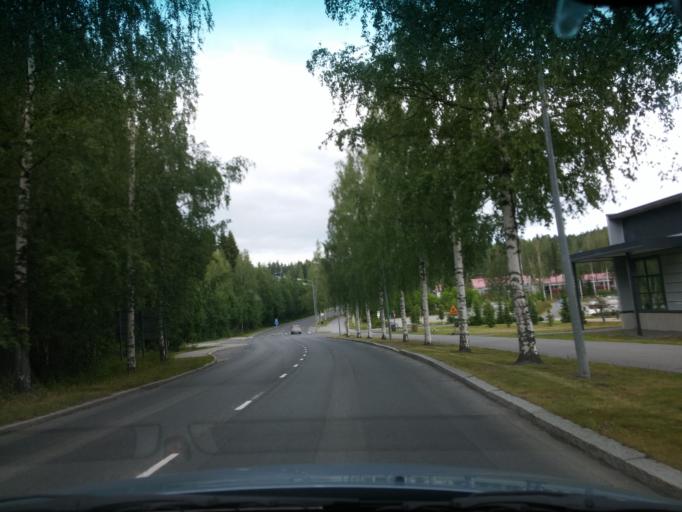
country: FI
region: Northern Savo
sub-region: Kuopio
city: Kuopio
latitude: 62.8393
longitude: 27.6565
